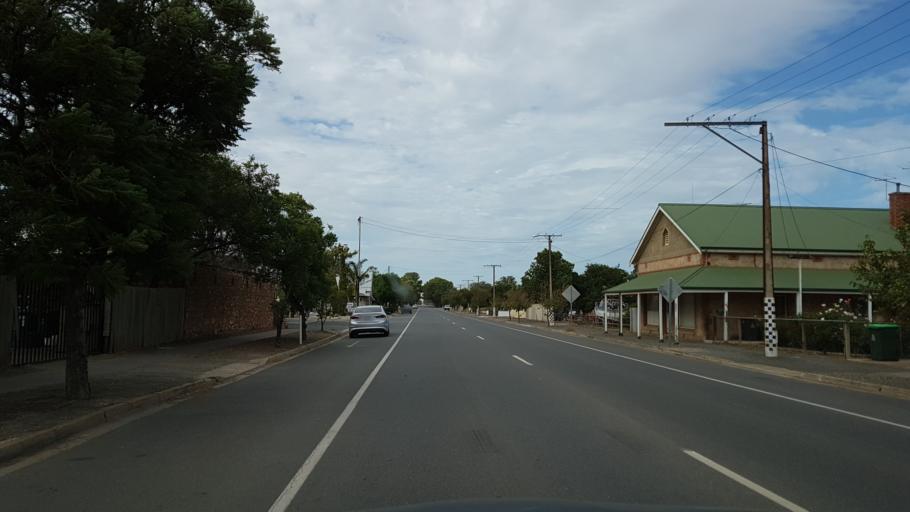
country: AU
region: South Australia
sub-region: Mallala
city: Mallala
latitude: -34.4386
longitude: 138.5098
